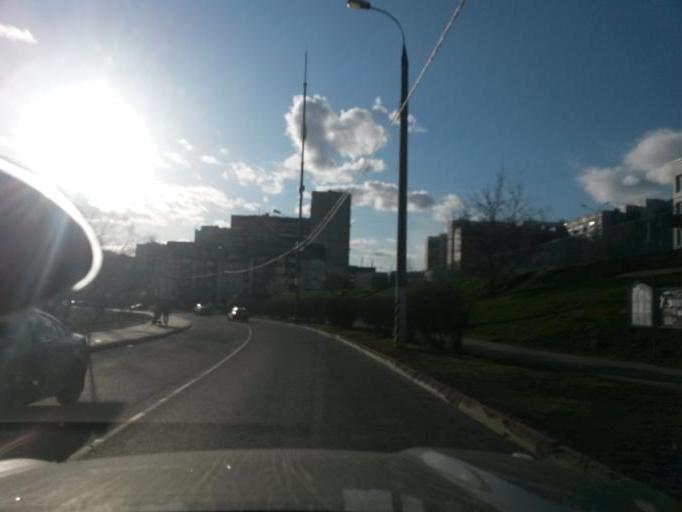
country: RU
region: Moscow
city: Annino
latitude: 55.5733
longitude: 37.5870
